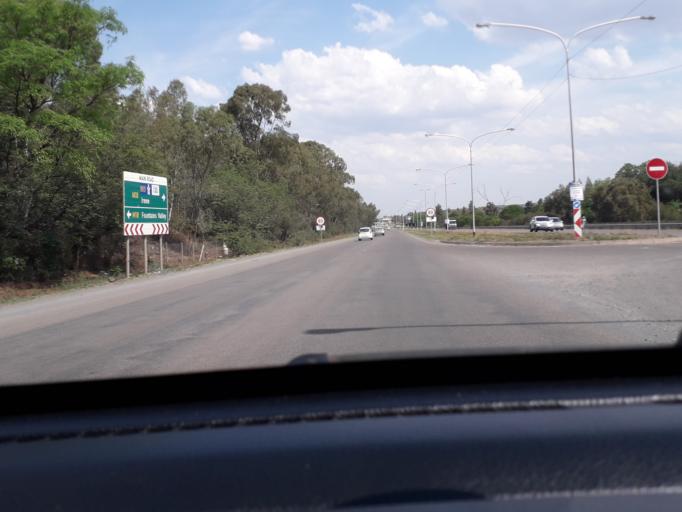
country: ZA
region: Gauteng
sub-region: City of Tshwane Metropolitan Municipality
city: Centurion
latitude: -25.8496
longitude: 28.2164
